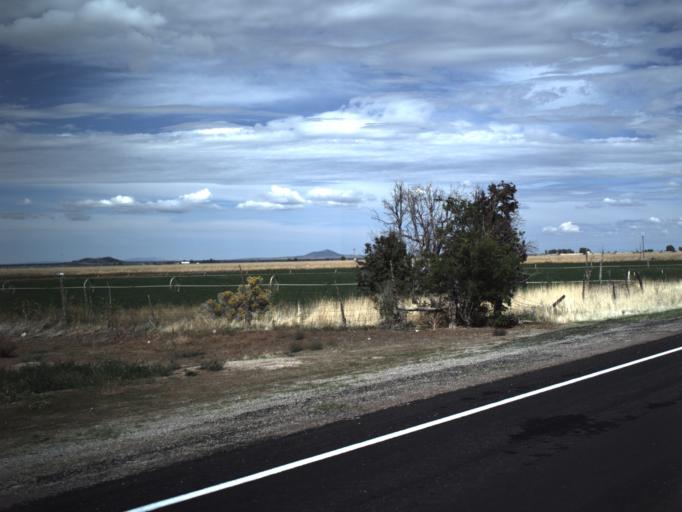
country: US
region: Utah
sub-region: Millard County
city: Fillmore
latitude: 38.8665
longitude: -112.4167
